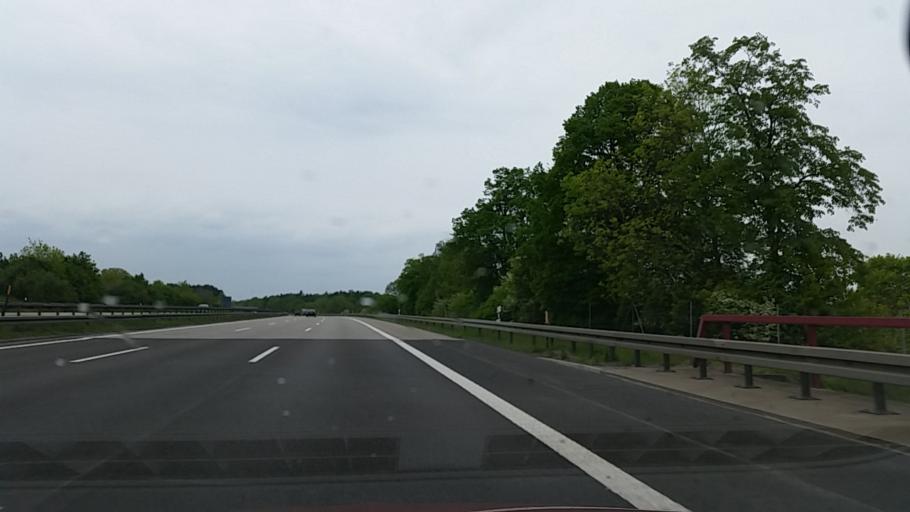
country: DE
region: Berlin
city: Hellersdorf
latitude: 52.5762
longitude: 13.6414
